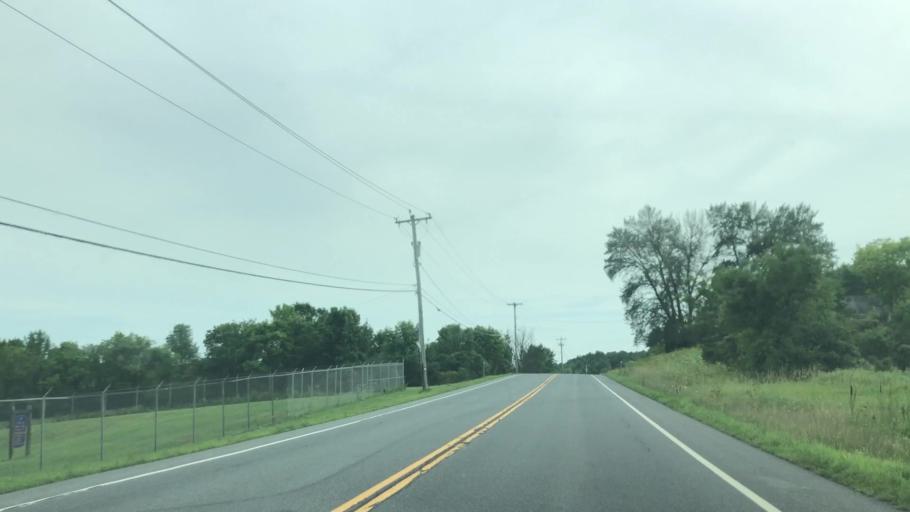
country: US
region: New York
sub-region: Washington County
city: Whitehall
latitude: 43.5313
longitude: -73.4118
